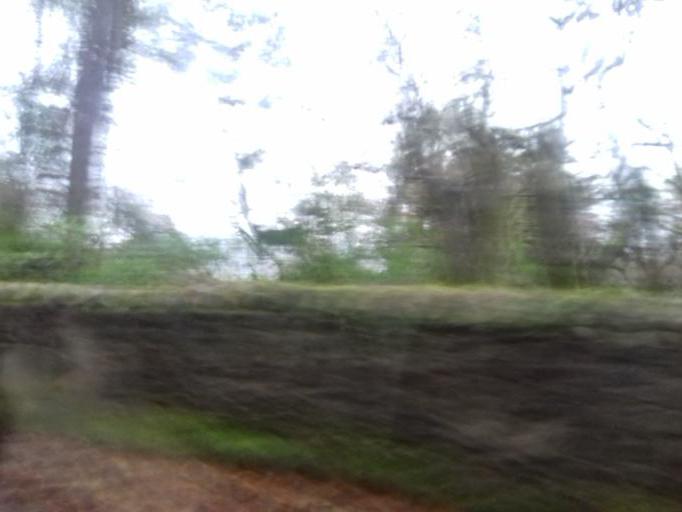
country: IE
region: Ulster
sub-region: County Donegal
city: Buncrana
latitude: 55.2175
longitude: -7.6131
